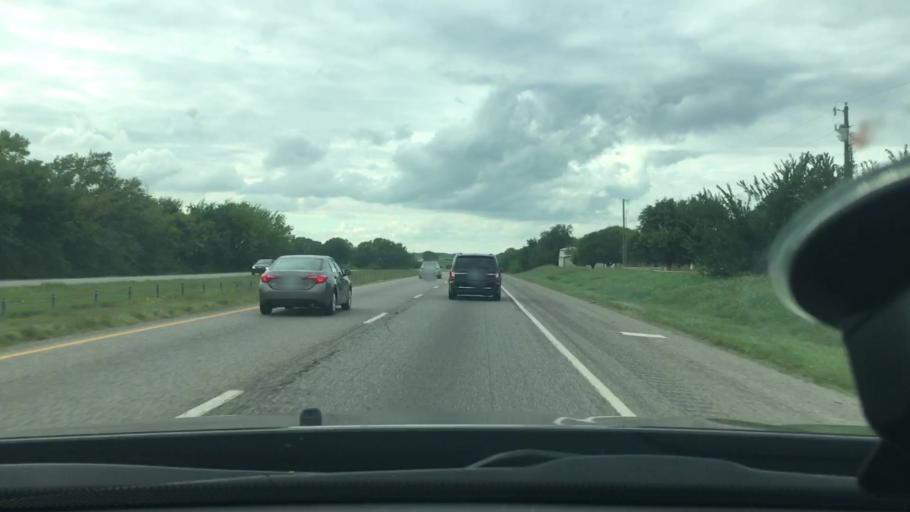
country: US
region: Oklahoma
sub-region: Cleveland County
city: Noble
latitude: 35.1087
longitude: -97.4355
